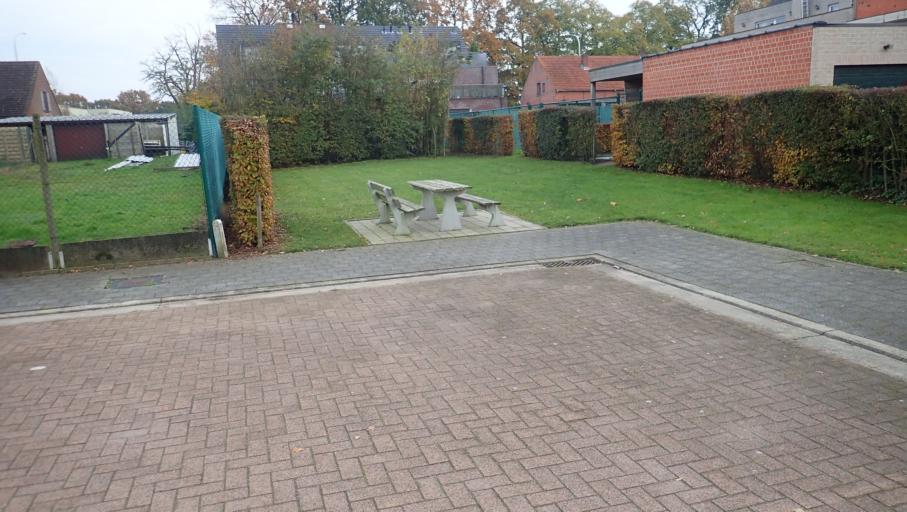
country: BE
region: Flanders
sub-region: Provincie Antwerpen
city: Wuustwezel
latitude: 51.3555
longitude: 4.5478
